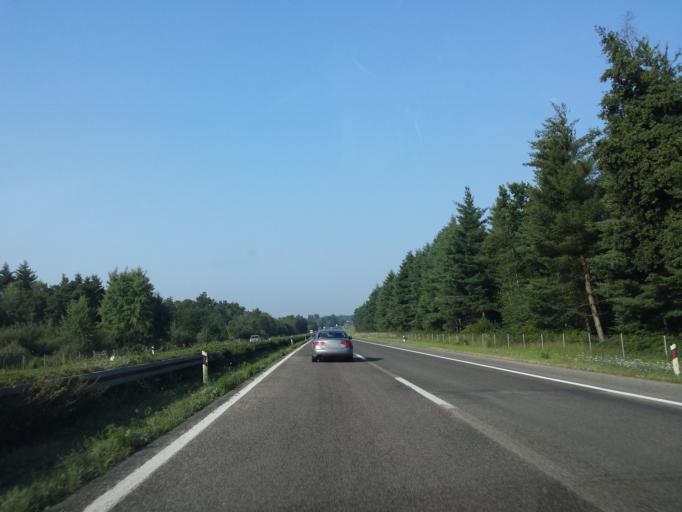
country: HR
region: Grad Zagreb
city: Horvati
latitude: 45.7050
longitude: 15.8477
